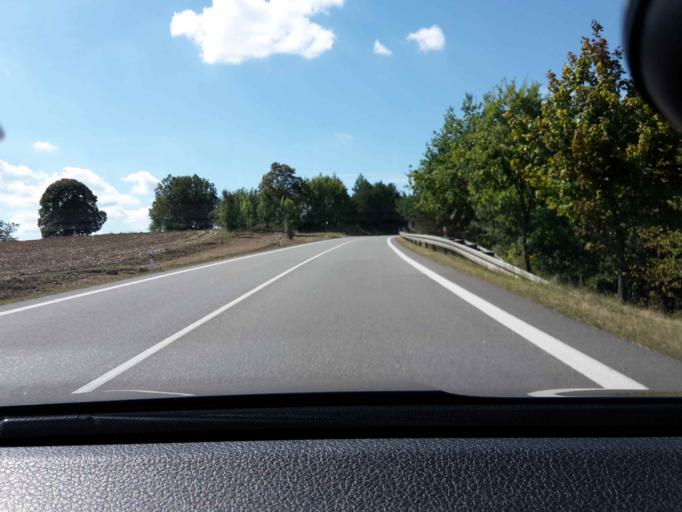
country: CZ
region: Jihocesky
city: Strmilov
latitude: 49.1559
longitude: 15.2034
